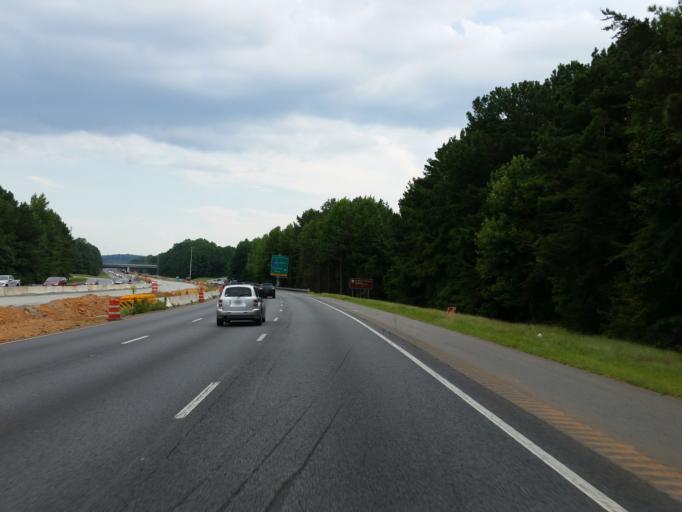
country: US
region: Georgia
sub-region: Cobb County
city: Kennesaw
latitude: 34.0449
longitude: -84.5637
